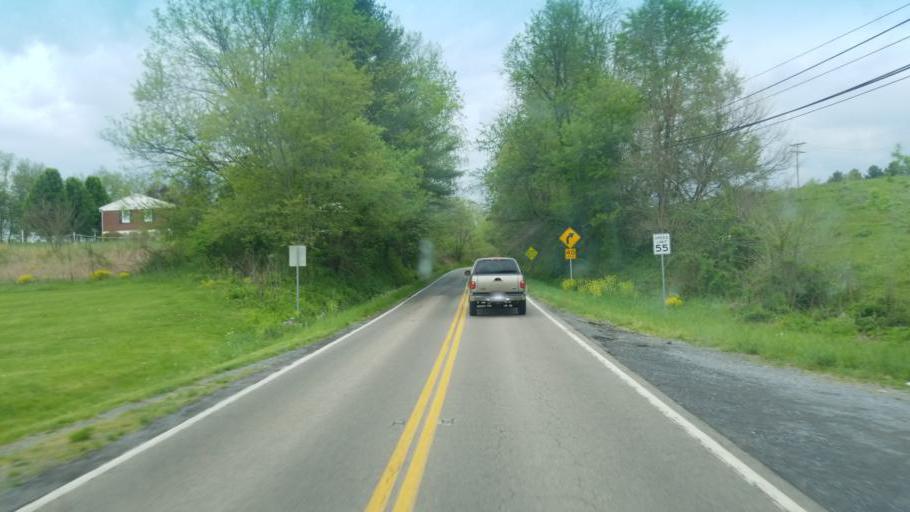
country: US
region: Virginia
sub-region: Smyth County
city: Chilhowie
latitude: 36.7890
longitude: -81.7004
